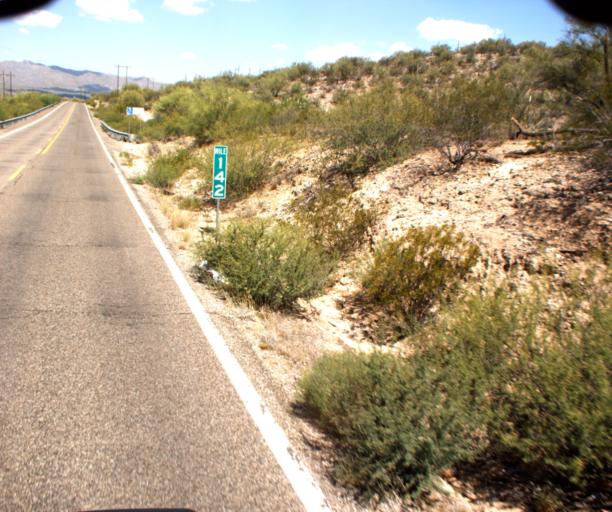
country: US
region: Arizona
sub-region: Pinal County
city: Kearny
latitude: 33.0219
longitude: -110.8549
